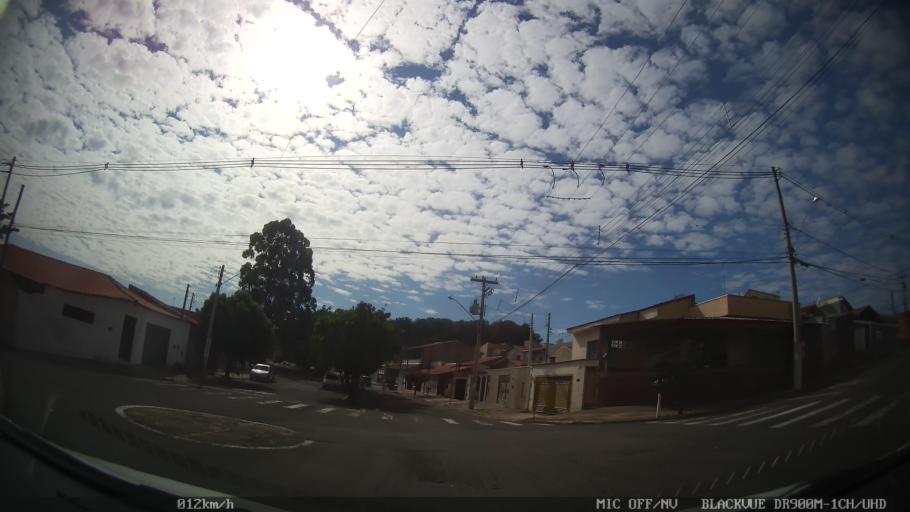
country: BR
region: Sao Paulo
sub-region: Santa Barbara D'Oeste
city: Santa Barbara d'Oeste
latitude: -22.7736
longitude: -47.3964
